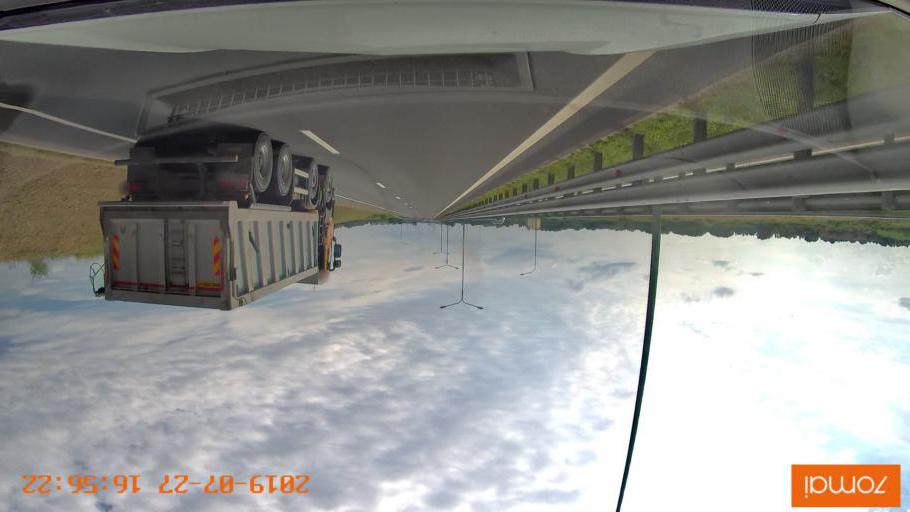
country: RU
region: Kaliningrad
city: Bol'shoe Isakovo
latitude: 54.6943
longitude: 20.7416
